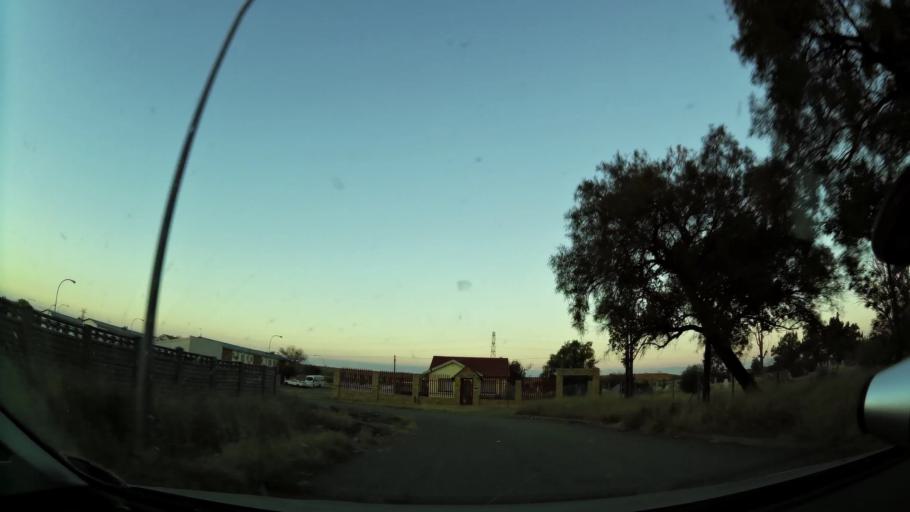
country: ZA
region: Northern Cape
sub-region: Frances Baard District Municipality
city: Kimberley
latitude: -28.7221
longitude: 24.7763
